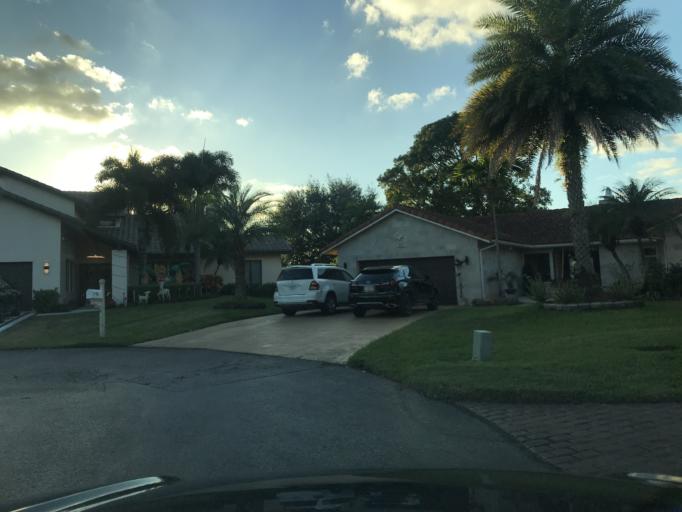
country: US
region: Florida
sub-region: Broward County
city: Pine Island Ridge
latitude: 26.1186
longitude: -80.2816
